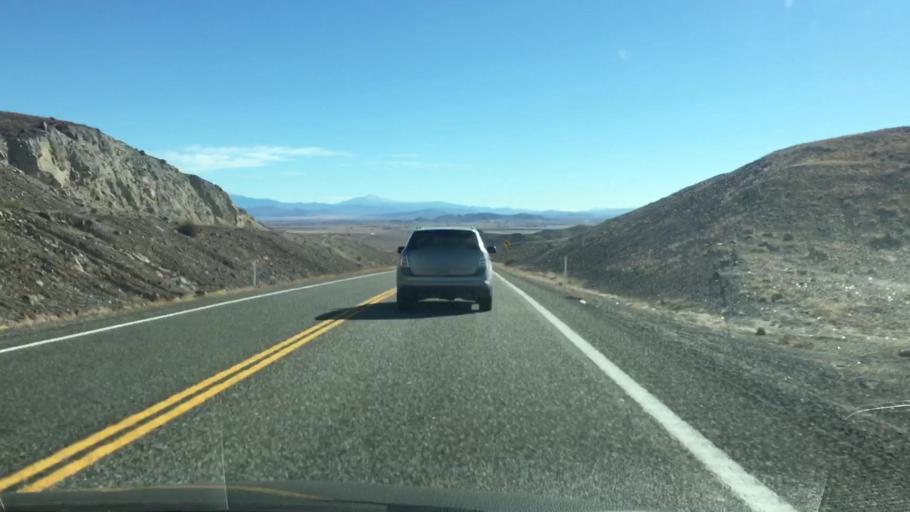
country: US
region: Nevada
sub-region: Lyon County
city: Yerington
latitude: 39.1778
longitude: -119.2075
